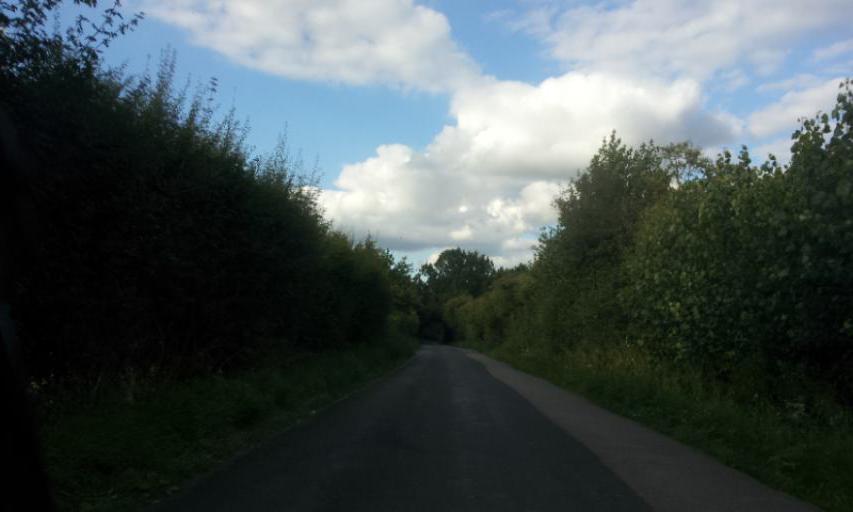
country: GB
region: England
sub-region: Kent
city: Headcorn
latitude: 51.1818
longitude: 0.6293
